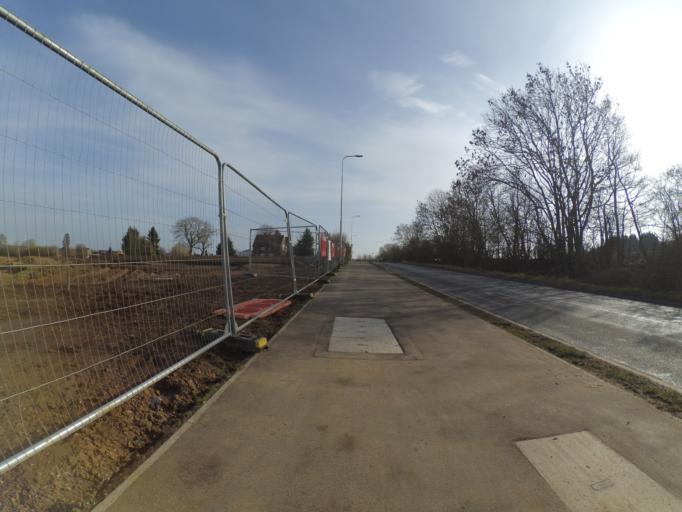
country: GB
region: England
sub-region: Warwickshire
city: Rugby
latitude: 52.3566
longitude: -1.1938
